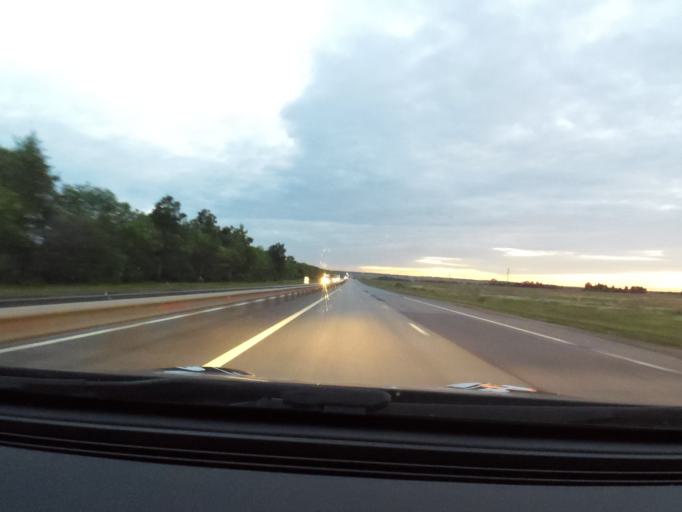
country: RU
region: Chuvashia
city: Yadrin
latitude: 55.9958
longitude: 46.1388
